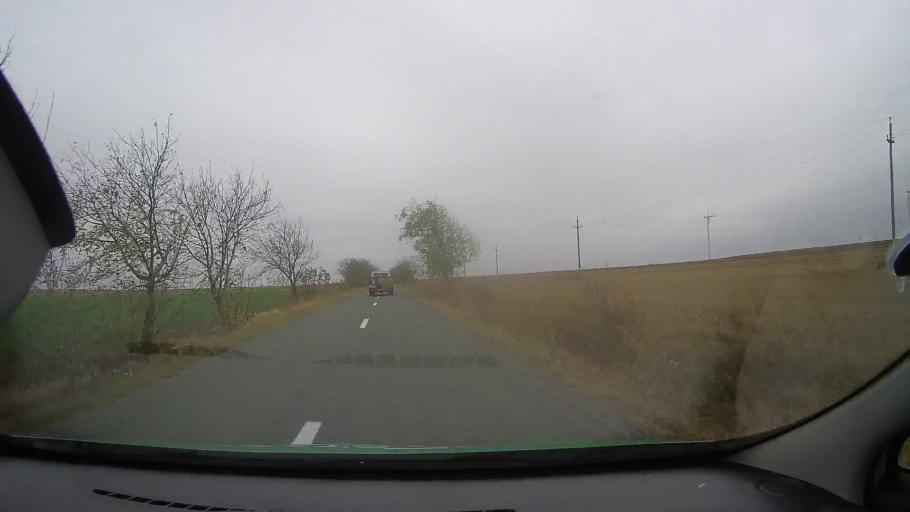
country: RO
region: Constanta
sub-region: Comuna Targusor
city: Targusor
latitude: 44.4772
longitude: 28.3782
